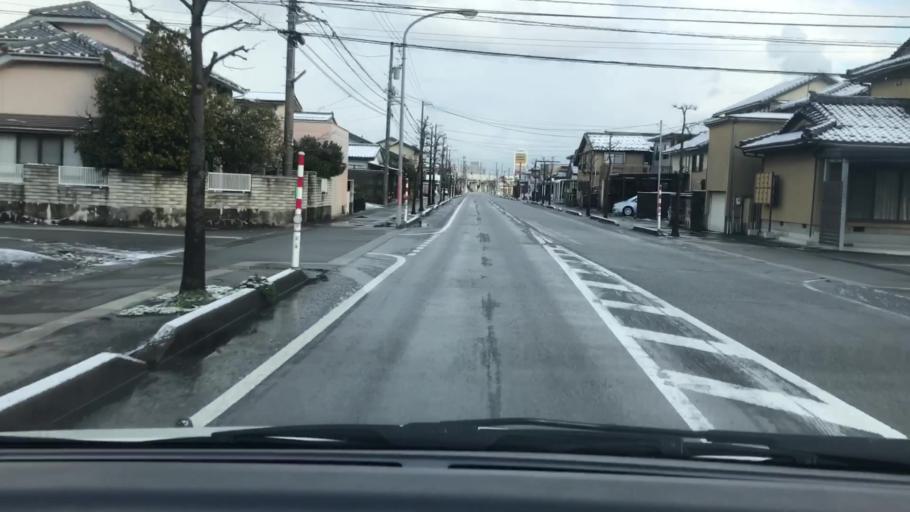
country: JP
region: Toyama
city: Toyama-shi
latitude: 36.7067
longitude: 137.2387
